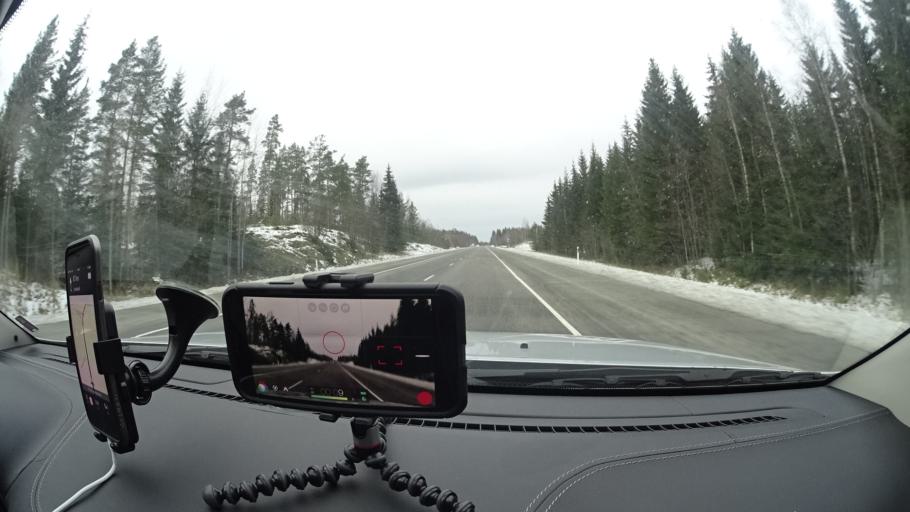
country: FI
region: Paijanne Tavastia
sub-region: Lahti
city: Heinola
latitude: 61.3223
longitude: 26.0422
